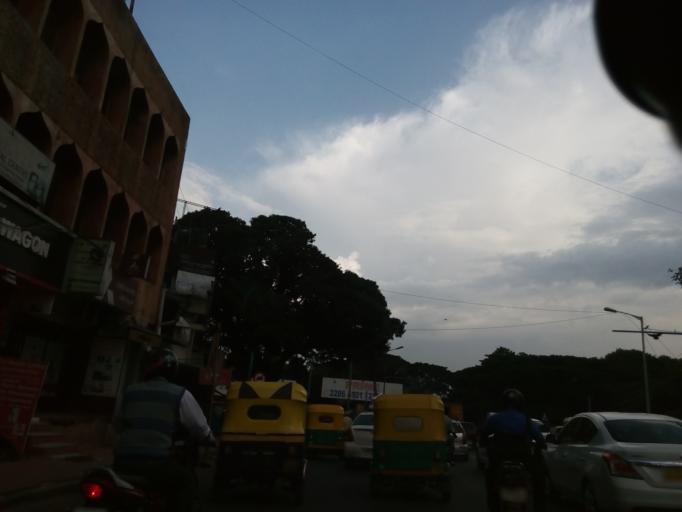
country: IN
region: Karnataka
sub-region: Bangalore Urban
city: Bangalore
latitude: 13.0059
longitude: 77.5932
